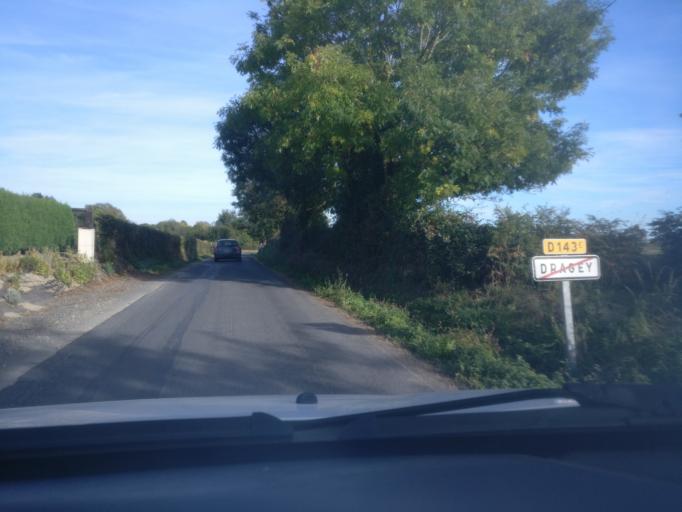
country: FR
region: Lower Normandy
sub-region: Departement de la Manche
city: Sartilly
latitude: 48.7114
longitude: -1.4885
